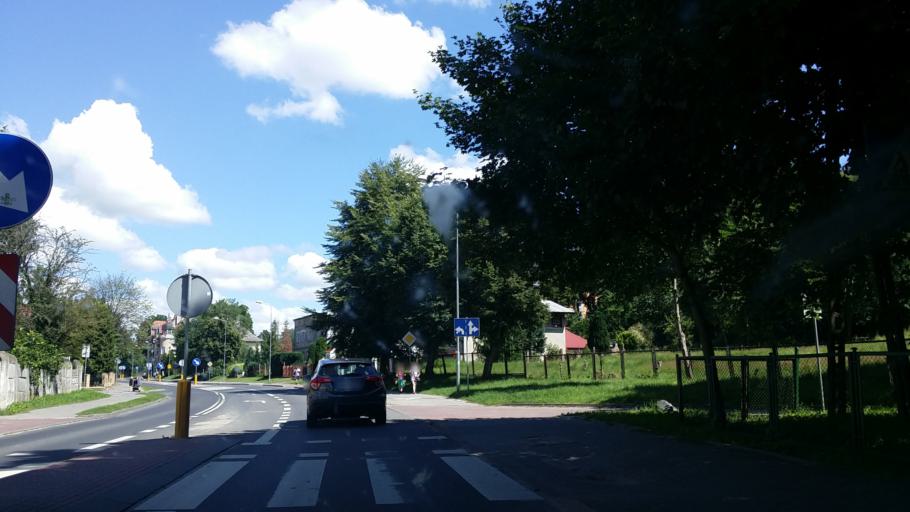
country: PL
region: West Pomeranian Voivodeship
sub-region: Powiat swidwinski
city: Swidwin
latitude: 53.7667
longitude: 15.7734
